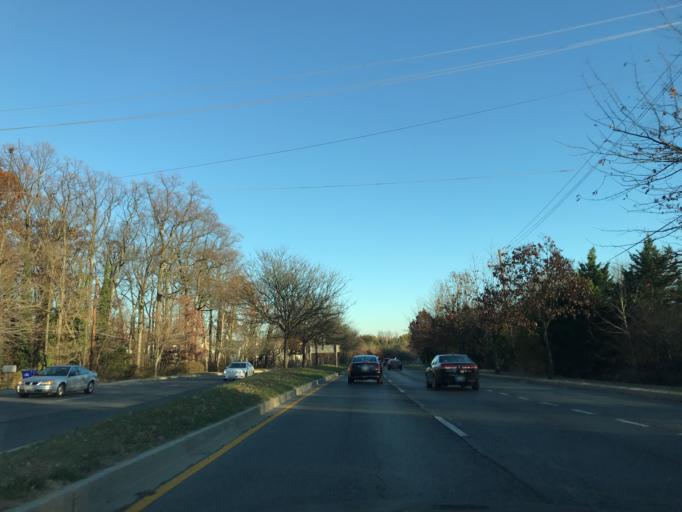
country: US
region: Maryland
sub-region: Montgomery County
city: Olney
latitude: 39.1494
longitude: -77.0572
